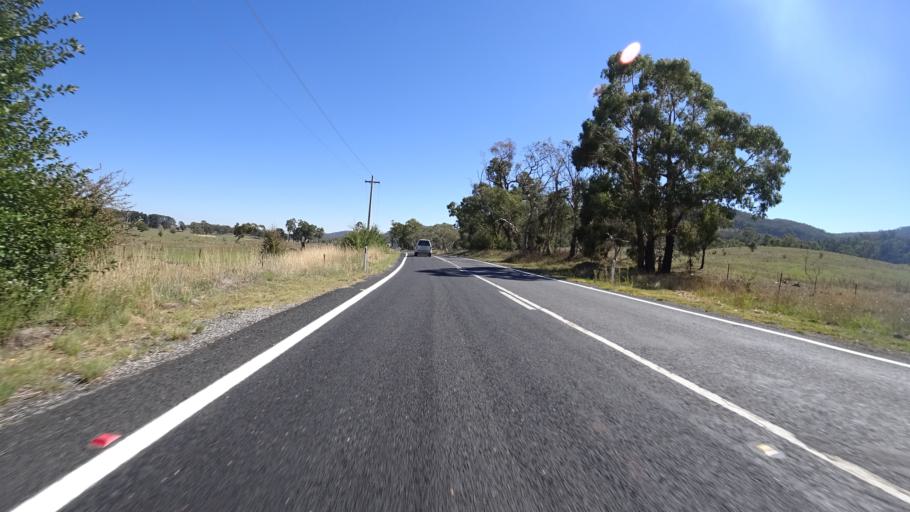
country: AU
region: New South Wales
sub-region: Lithgow
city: Portland
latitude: -33.3129
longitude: 150.0356
